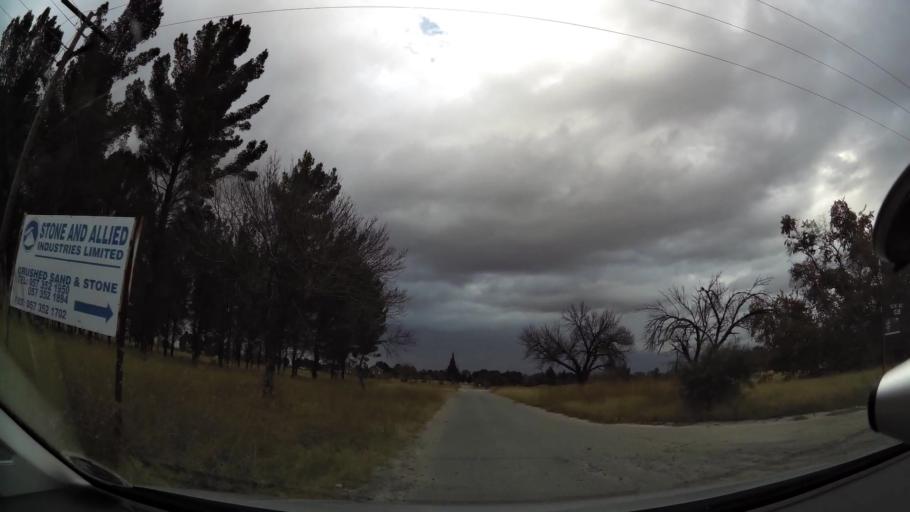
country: ZA
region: Orange Free State
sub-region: Lejweleputswa District Municipality
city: Welkom
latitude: -27.9702
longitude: 26.7008
